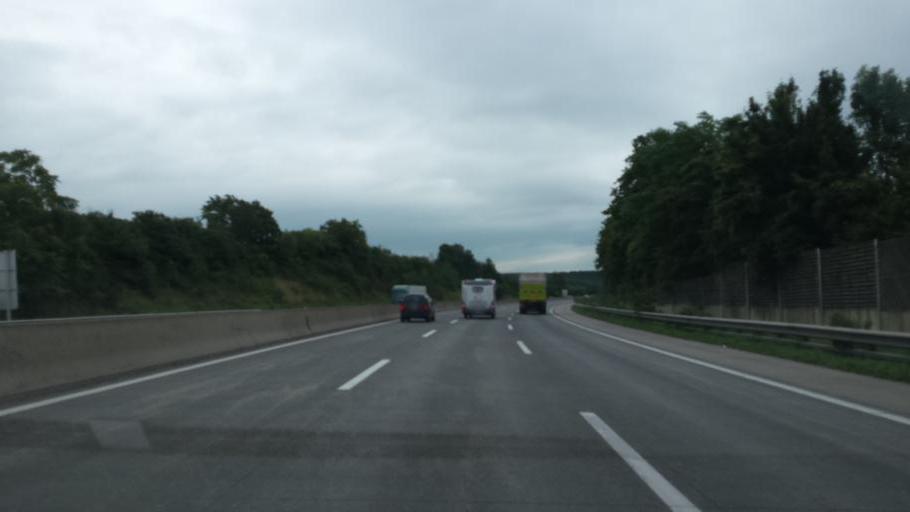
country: AT
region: Lower Austria
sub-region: Politischer Bezirk Melk
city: Melk
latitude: 48.2139
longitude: 15.3573
